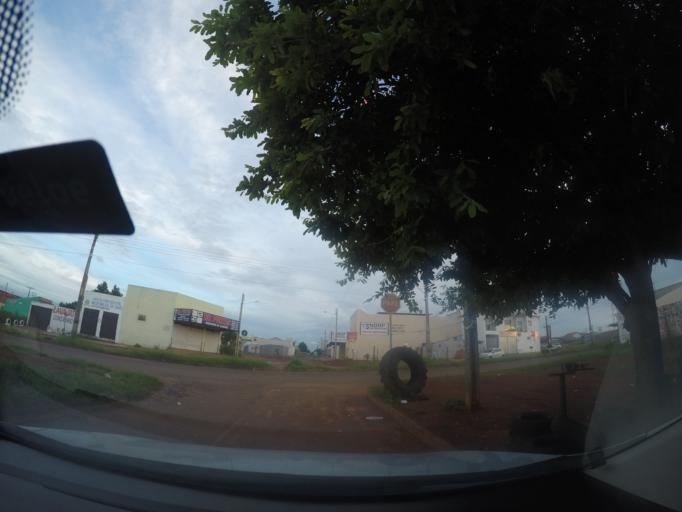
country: BR
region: Goias
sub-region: Goianira
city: Goianira
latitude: -16.5725
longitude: -49.3813
